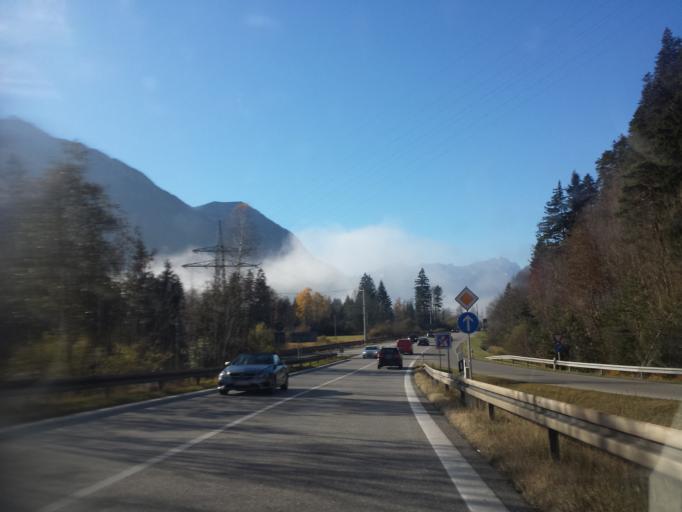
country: DE
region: Bavaria
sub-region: Upper Bavaria
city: Eschenlohe
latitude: 47.5877
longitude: 11.1752
